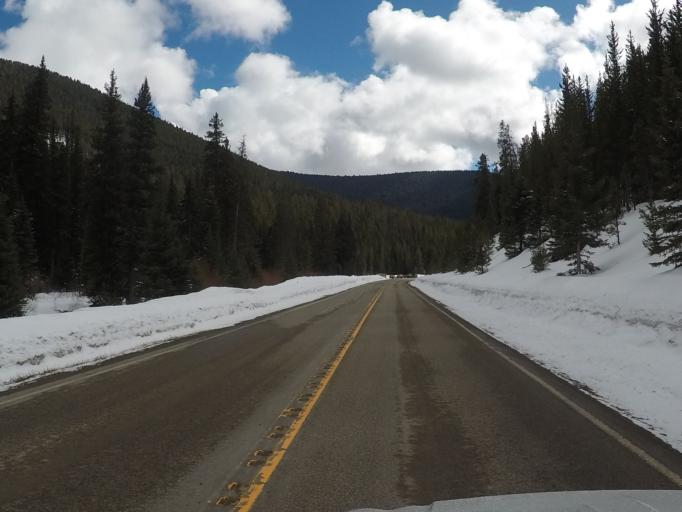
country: US
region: Montana
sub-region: Meagher County
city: White Sulphur Springs
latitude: 46.7858
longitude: -110.6970
